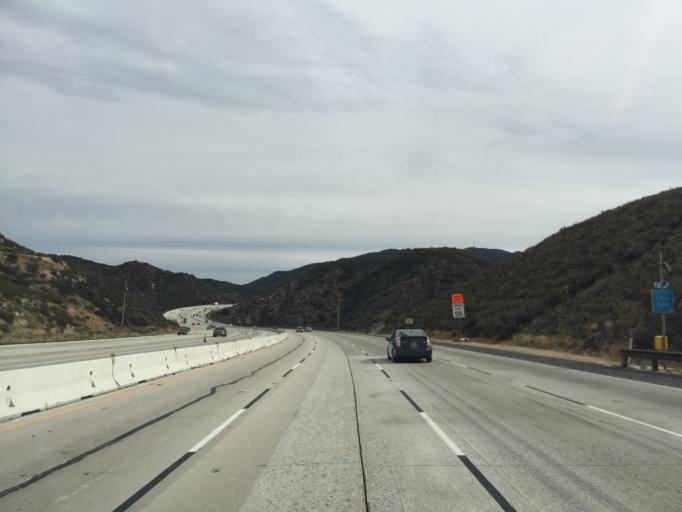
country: US
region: California
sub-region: Los Angeles County
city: Burbank
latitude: 34.2434
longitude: -118.3181
